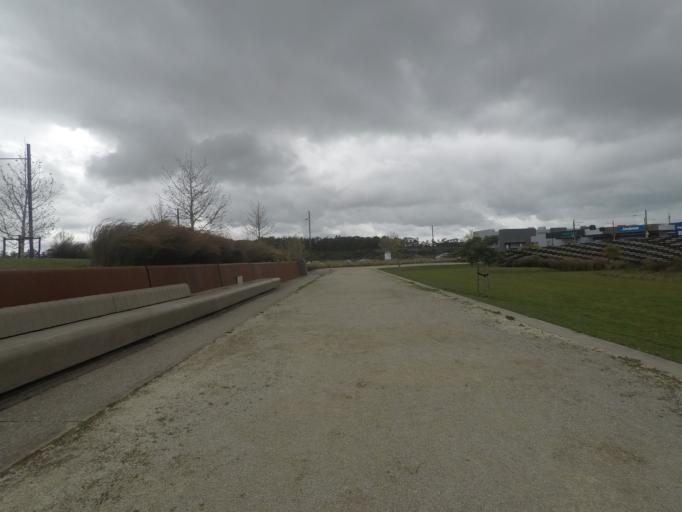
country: NZ
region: Auckland
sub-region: Auckland
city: Rosebank
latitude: -36.8117
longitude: 174.6065
